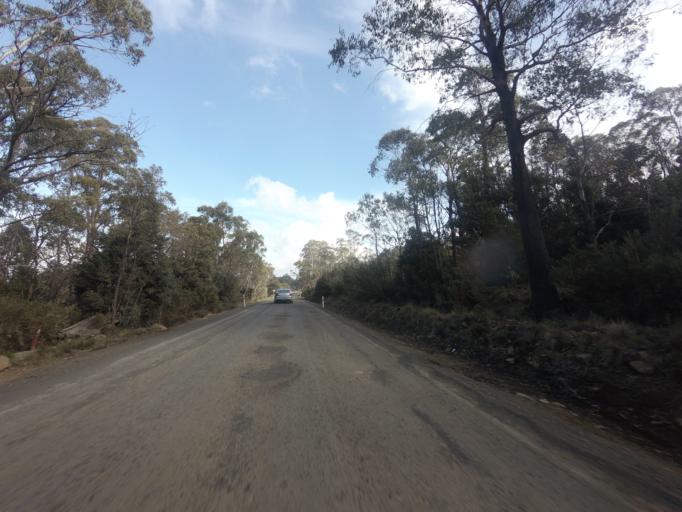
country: AU
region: Tasmania
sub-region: Meander Valley
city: Deloraine
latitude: -41.7815
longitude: 146.7064
